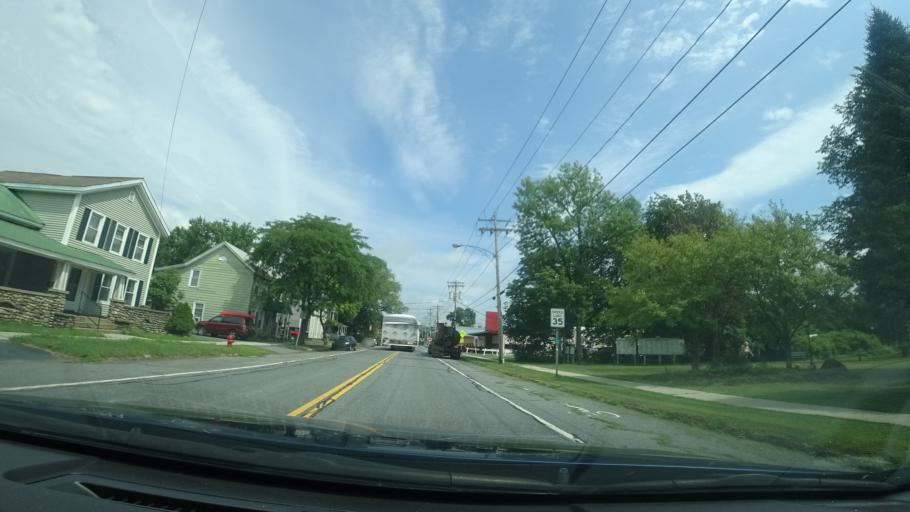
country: US
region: New York
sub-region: Warren County
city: Queensbury
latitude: 43.4128
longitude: -73.4883
